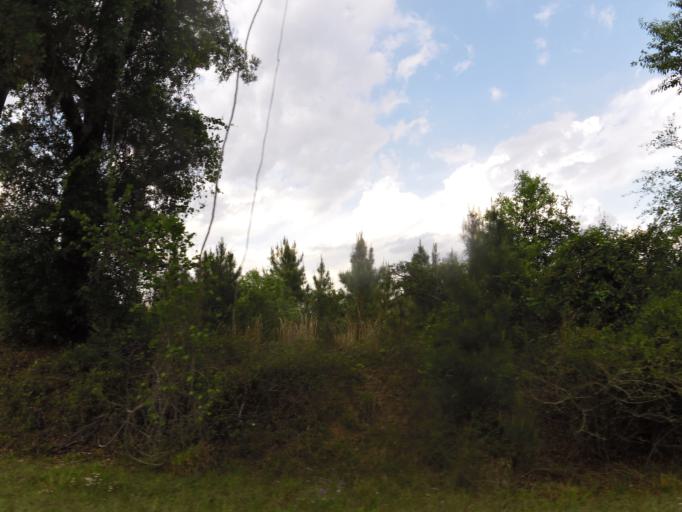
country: US
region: Georgia
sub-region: Charlton County
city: Folkston
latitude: 30.8080
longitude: -82.0566
